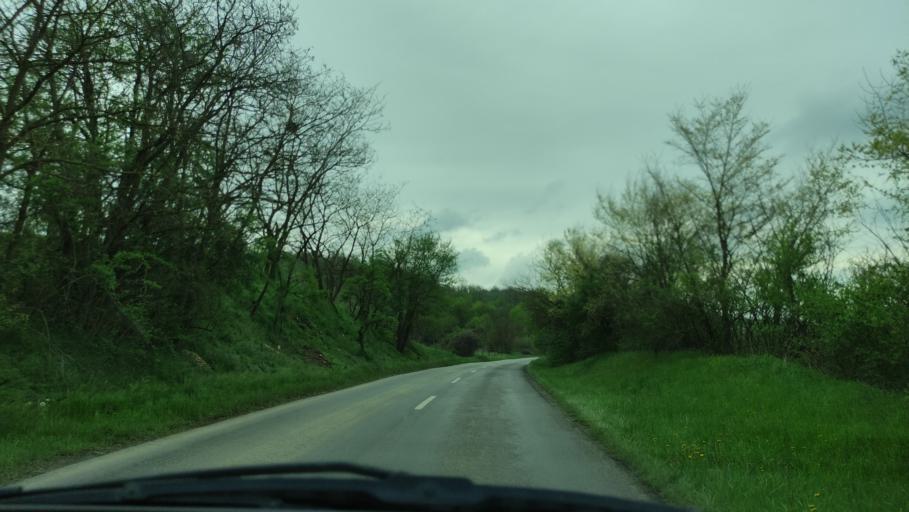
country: HU
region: Baranya
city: Komlo
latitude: 46.2259
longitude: 18.2335
